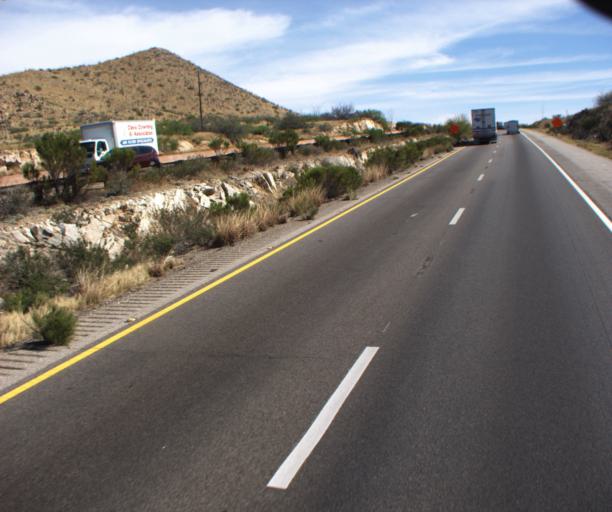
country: US
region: Arizona
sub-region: Cochise County
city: Saint David
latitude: 32.0131
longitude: -110.1218
